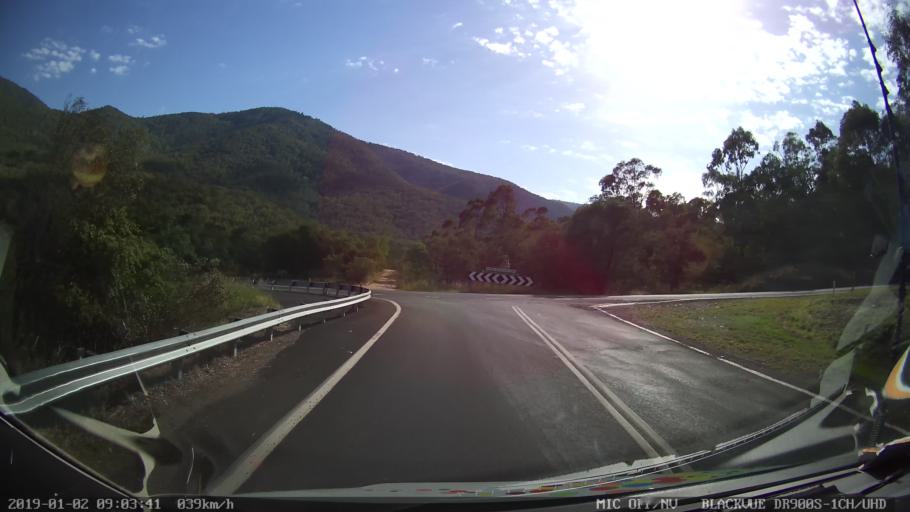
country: AU
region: New South Wales
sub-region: Tumut Shire
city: Tumut
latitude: -35.5681
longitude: 148.3256
